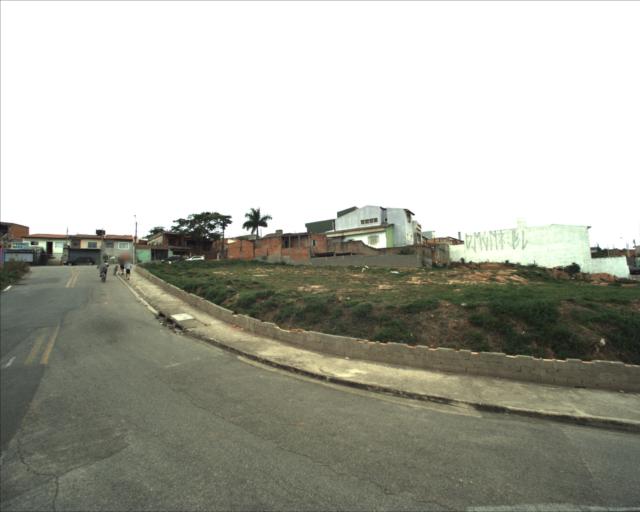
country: BR
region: Sao Paulo
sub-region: Sorocaba
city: Sorocaba
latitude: -23.4907
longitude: -47.4890
